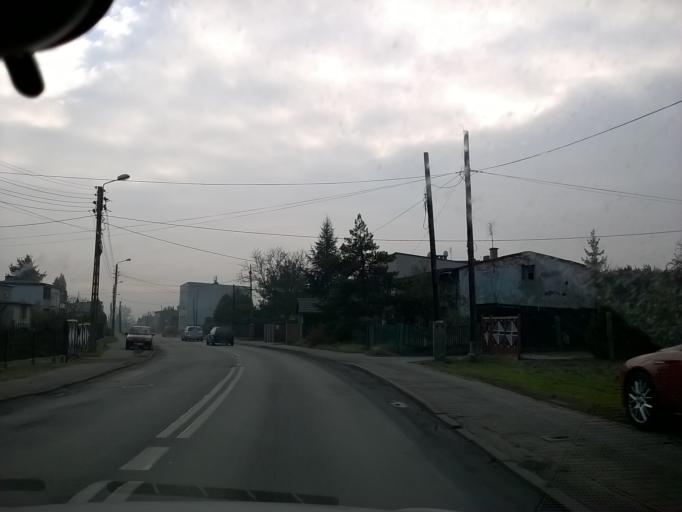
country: PL
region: Silesian Voivodeship
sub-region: Ruda Slaska
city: Ruda Slaska
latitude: 50.2515
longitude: 18.8382
